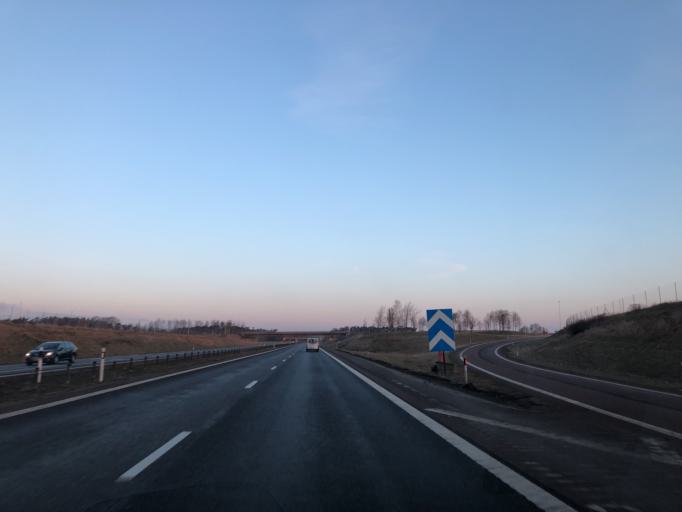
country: SE
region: Halland
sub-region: Laholms Kommun
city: Mellbystrand
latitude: 56.4497
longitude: 12.9510
